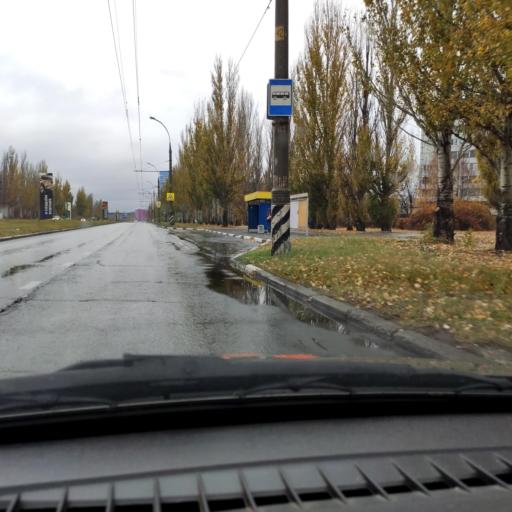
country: RU
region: Samara
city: Tol'yatti
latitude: 53.5483
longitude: 49.2731
